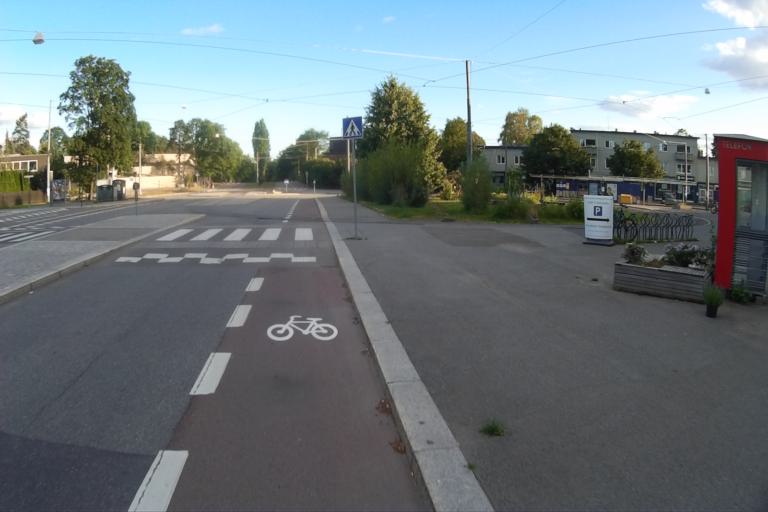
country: NO
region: Oslo
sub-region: Oslo
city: Oslo
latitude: 59.9408
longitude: 10.7296
